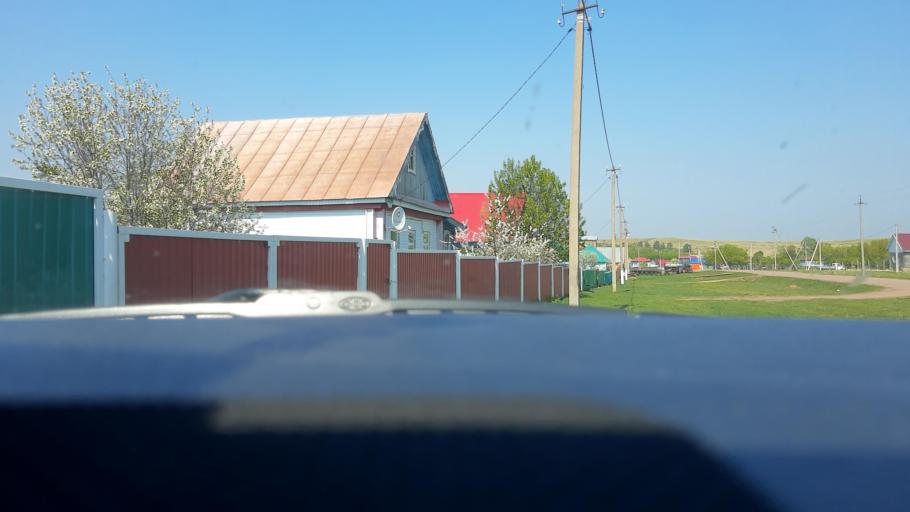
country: RU
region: Bashkortostan
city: Chishmy
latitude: 54.4506
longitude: 55.3221
